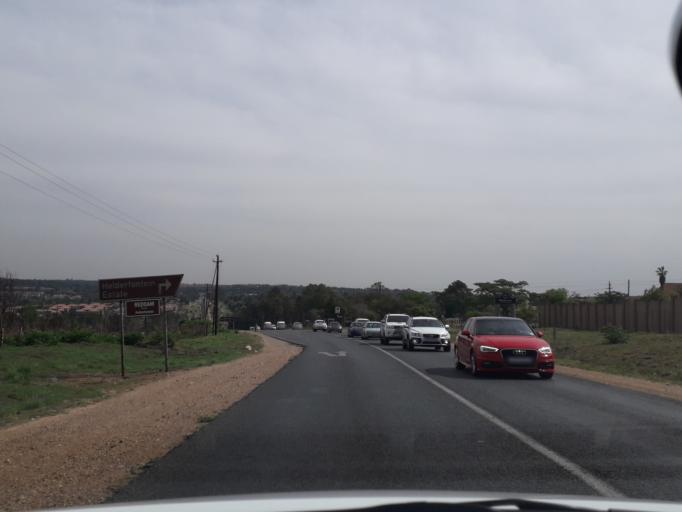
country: ZA
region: Gauteng
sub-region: City of Johannesburg Metropolitan Municipality
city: Diepsloot
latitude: -26.0028
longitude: 28.0413
